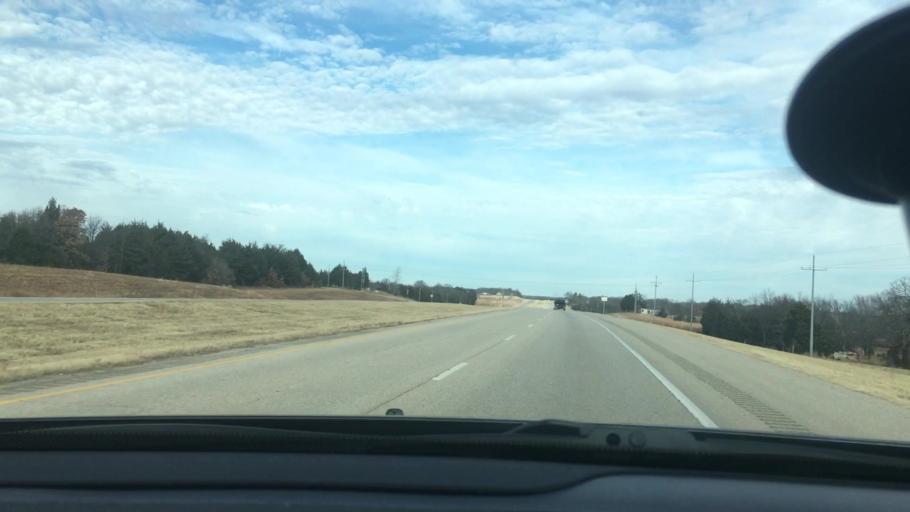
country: US
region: Oklahoma
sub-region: Pontotoc County
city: Byng
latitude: 34.9027
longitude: -96.6755
